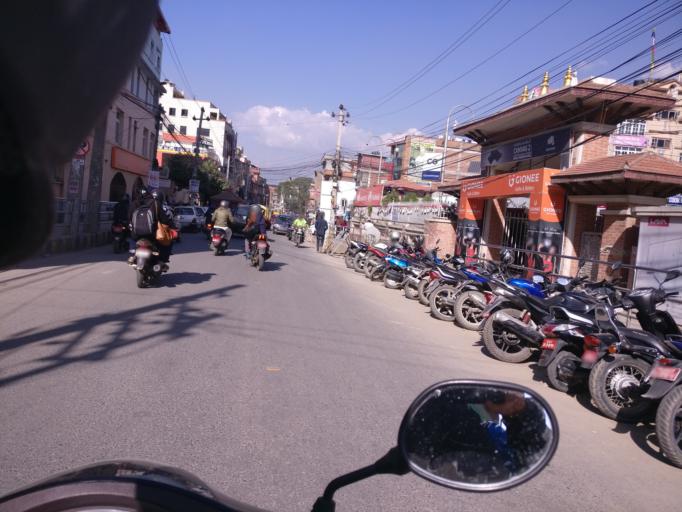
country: NP
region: Central Region
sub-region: Bagmati Zone
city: Patan
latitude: 27.6676
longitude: 85.3215
